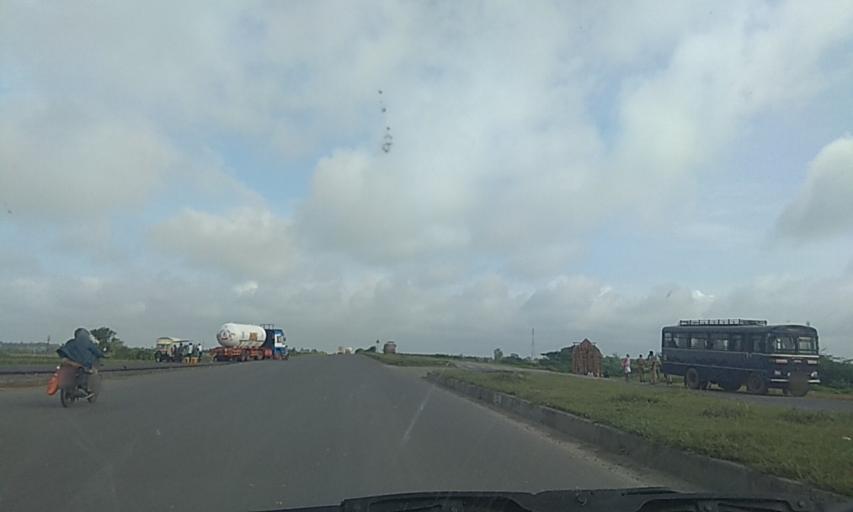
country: IN
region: Karnataka
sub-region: Haveri
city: Haveri
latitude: 14.8614
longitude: 75.3225
